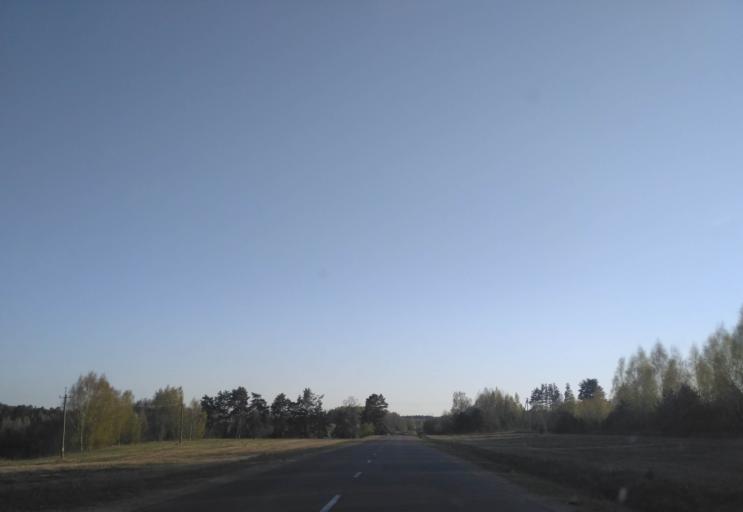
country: BY
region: Minsk
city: Radashkovichy
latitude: 54.1455
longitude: 27.2128
